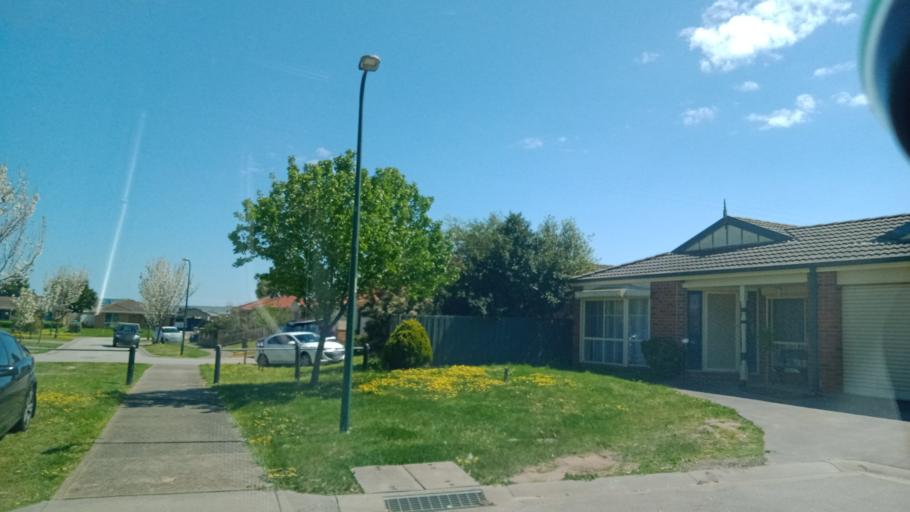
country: AU
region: Victoria
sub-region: Casey
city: Cranbourne West
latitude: -38.0926
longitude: 145.2574
